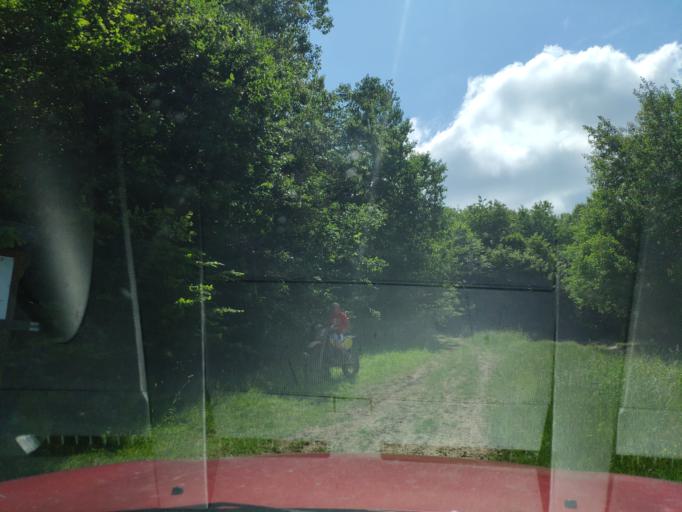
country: SK
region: Presovsky
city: Vranov nad Topl'ou
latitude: 48.8215
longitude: 21.6048
